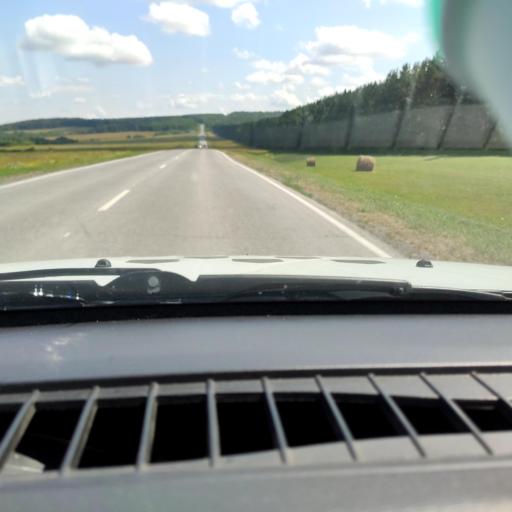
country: RU
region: Bashkortostan
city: Verkhniye Kigi
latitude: 55.3947
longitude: 58.6454
